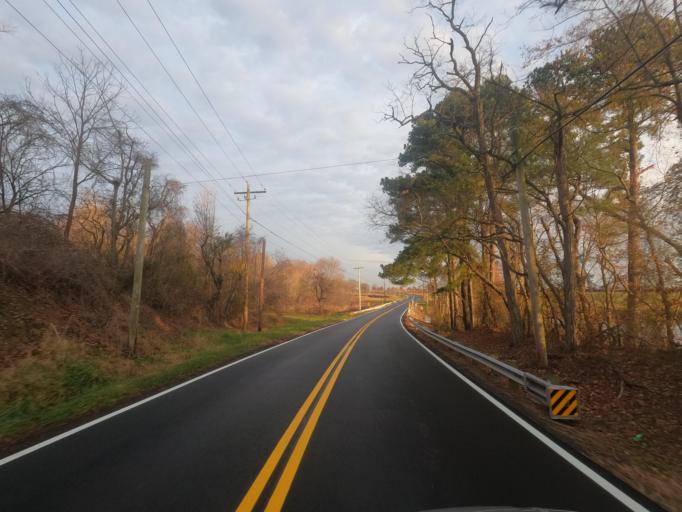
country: US
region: Delaware
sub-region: New Castle County
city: Townsend
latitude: 39.2708
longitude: -75.8379
